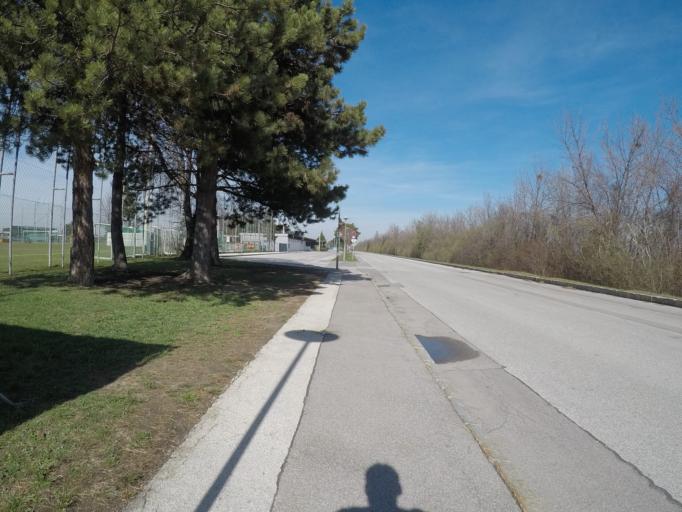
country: AT
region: Lower Austria
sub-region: Politischer Bezirk Modling
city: Vosendorf
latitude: 48.1141
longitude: 16.3357
